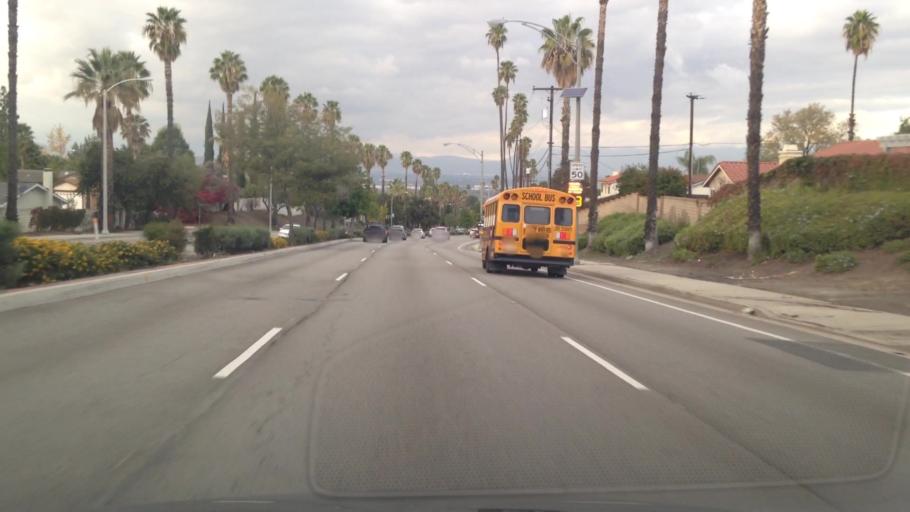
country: US
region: California
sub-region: Riverside County
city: Riverside
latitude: 33.9376
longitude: -117.3514
